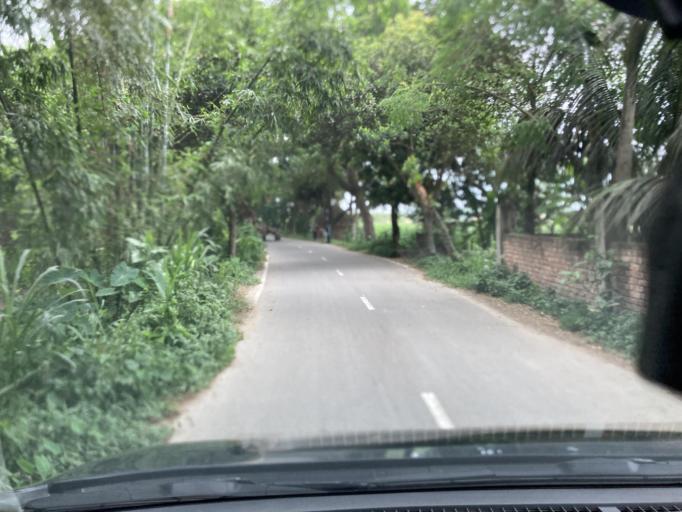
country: BD
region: Dhaka
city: Dohar
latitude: 23.7730
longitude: 90.0662
